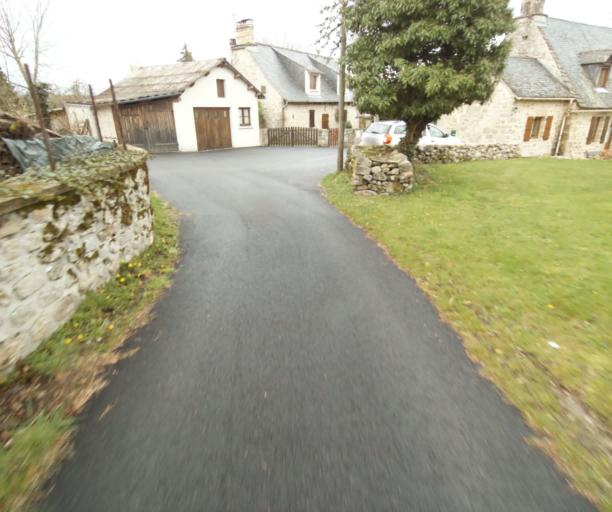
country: FR
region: Limousin
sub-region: Departement de la Correze
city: Saint-Privat
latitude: 45.2203
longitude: 2.0230
